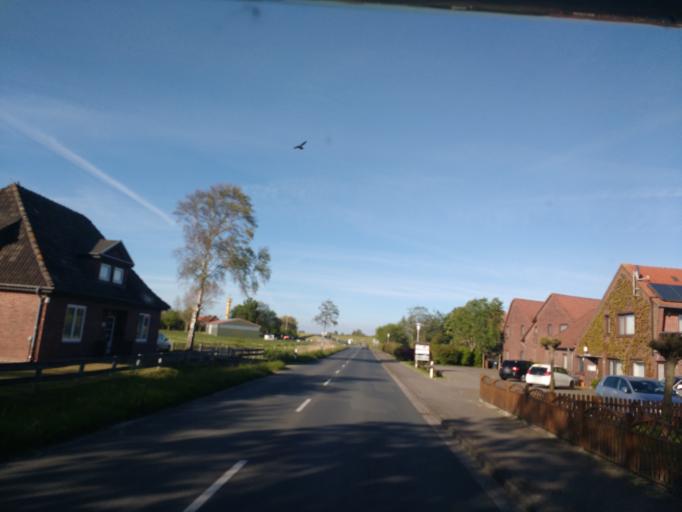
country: DE
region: Lower Saxony
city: Schillig
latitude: 53.6973
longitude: 8.0151
